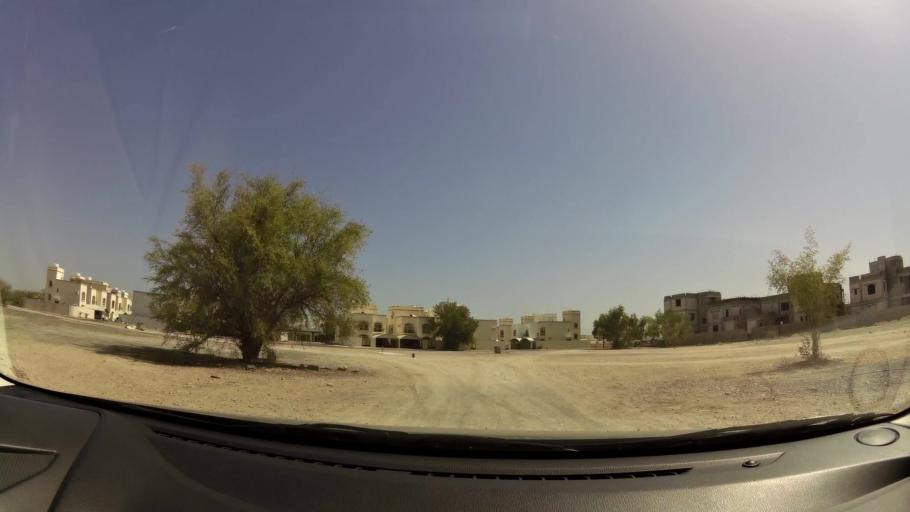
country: OM
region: Muhafazat Masqat
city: As Sib al Jadidah
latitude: 23.5979
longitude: 58.2431
